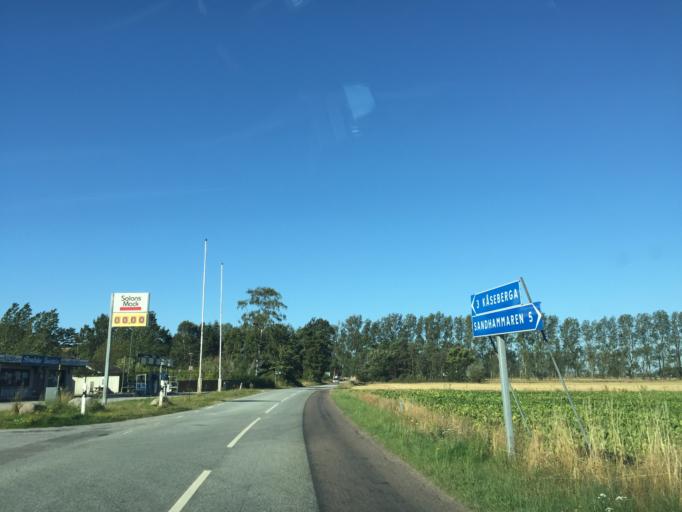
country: SE
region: Skane
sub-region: Ystads Kommun
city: Kopingebro
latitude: 55.3919
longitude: 14.1106
